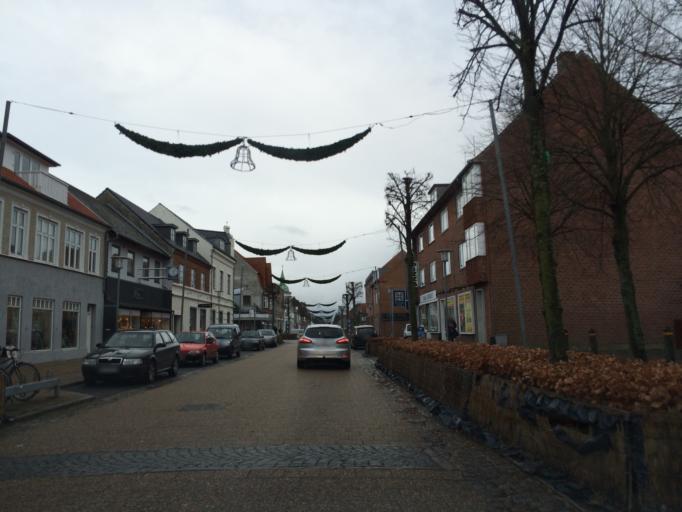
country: DK
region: Central Jutland
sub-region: Ringkobing-Skjern Kommune
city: Skjern
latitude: 55.9489
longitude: 8.4915
